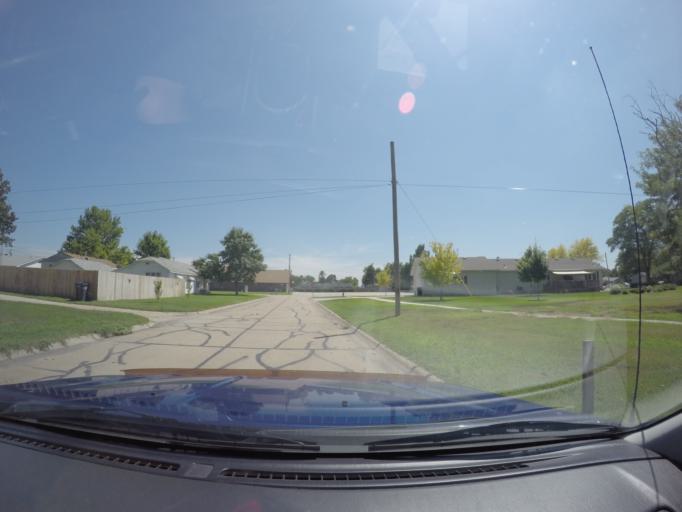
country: US
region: Nebraska
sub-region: Harlan County
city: Alma
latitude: 40.0980
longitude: -99.3672
